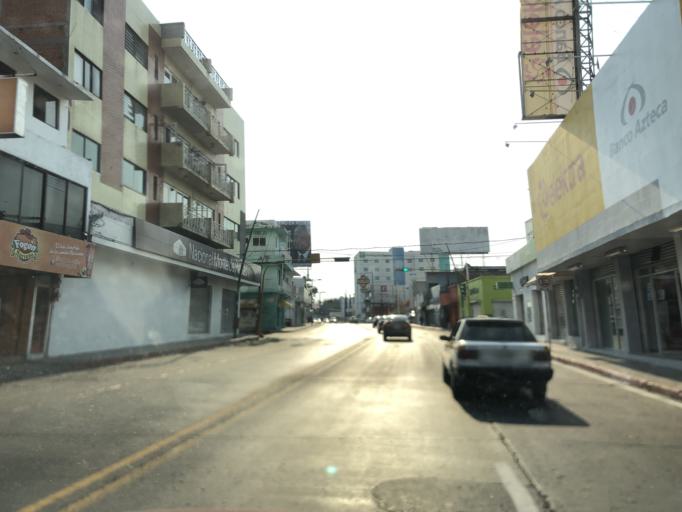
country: MX
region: Chiapas
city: Tuxtla Gutierrez
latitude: 16.7549
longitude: -93.1244
